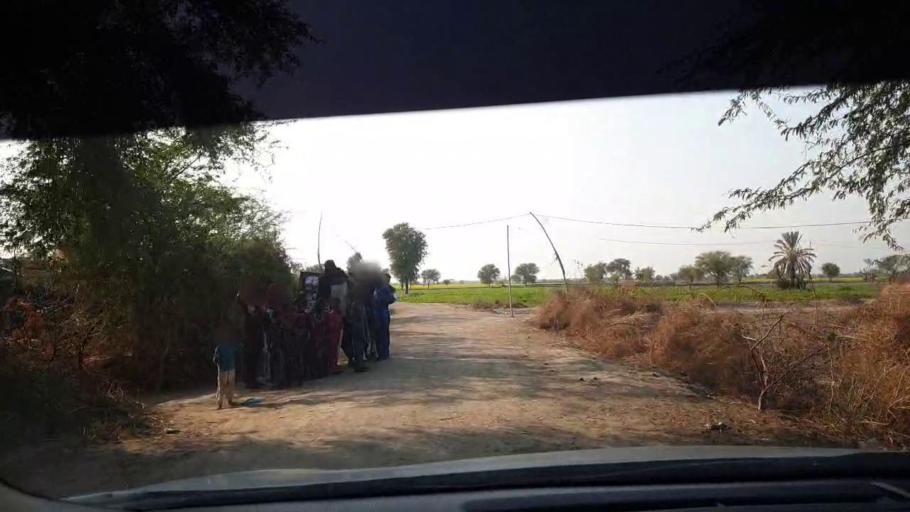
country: PK
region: Sindh
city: Berani
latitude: 25.8298
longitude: 68.7696
